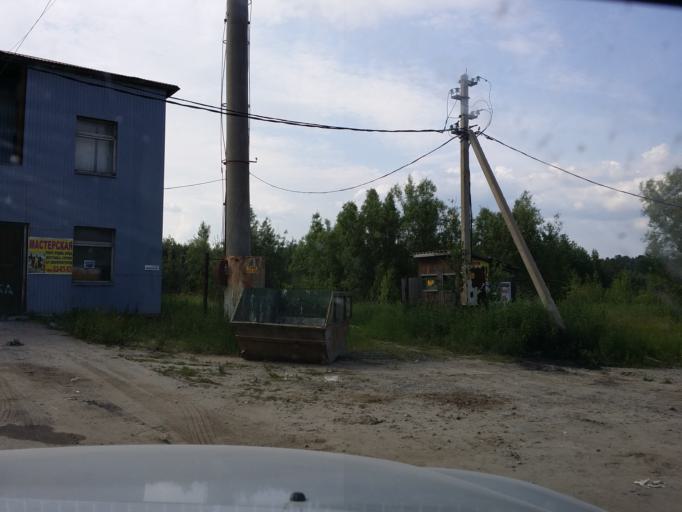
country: RU
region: Khanty-Mansiyskiy Avtonomnyy Okrug
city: Nizhnevartovsk
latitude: 60.9766
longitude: 76.5160
